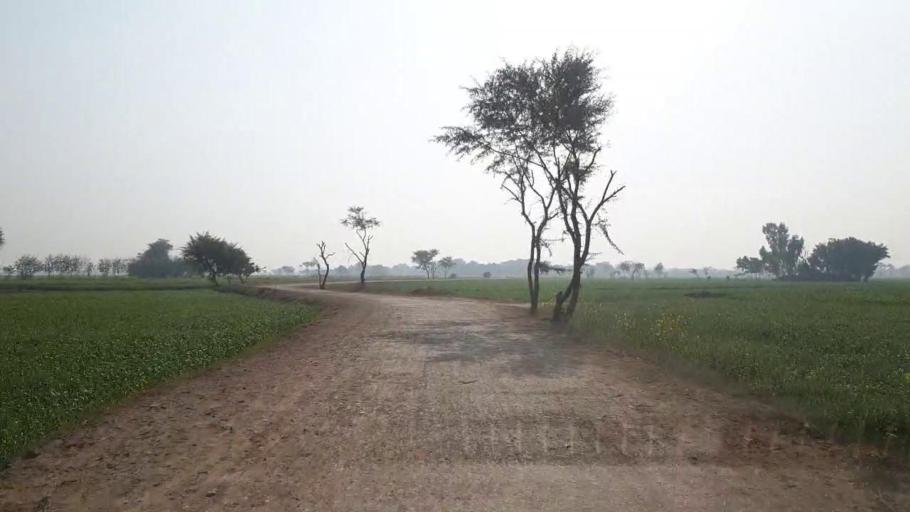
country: PK
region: Sindh
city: Bhit Shah
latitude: 25.7338
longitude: 68.5204
